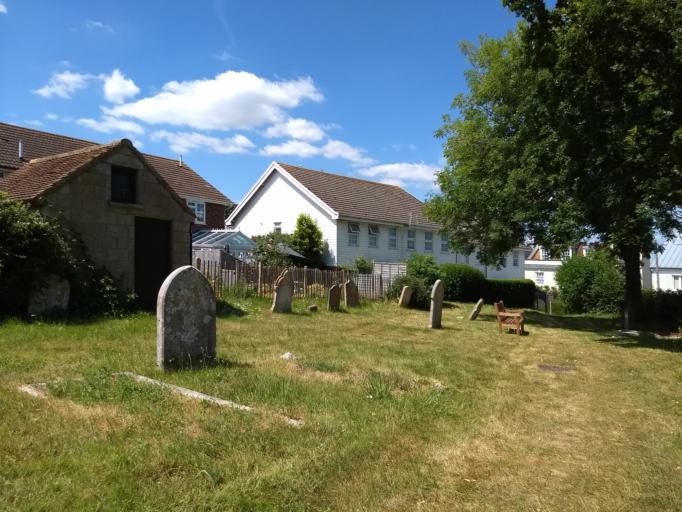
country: GB
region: England
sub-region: Isle of Wight
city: Yarmouth
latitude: 50.7060
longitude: -1.4947
